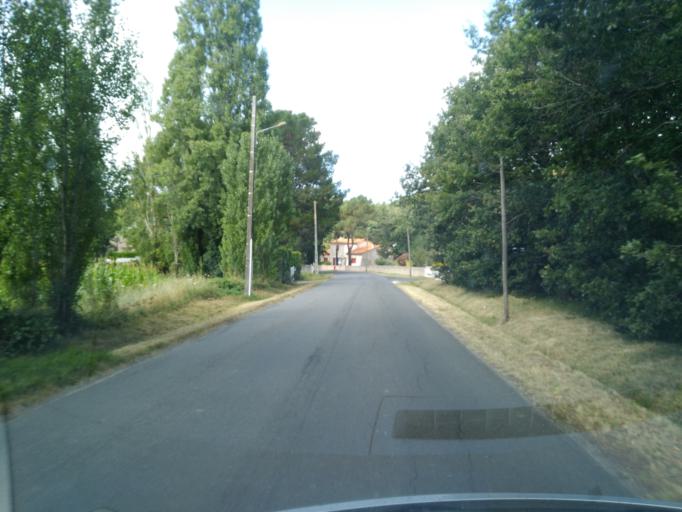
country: FR
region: Poitou-Charentes
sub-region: Departement de la Charente-Maritime
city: Breuillet
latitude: 45.6863
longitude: -1.0756
